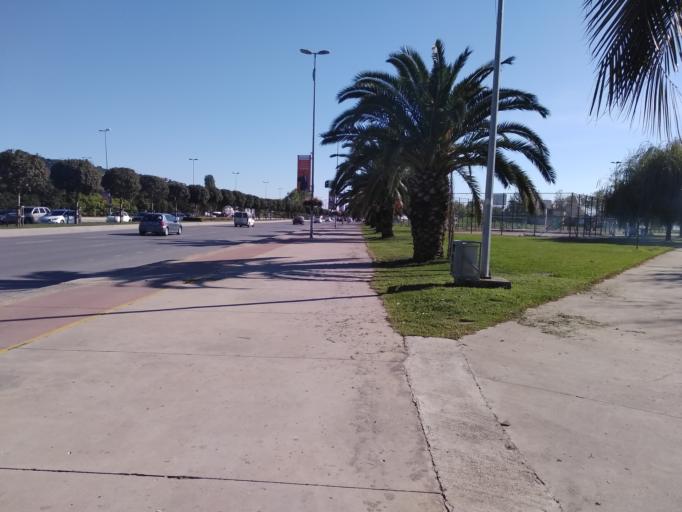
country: TR
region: Istanbul
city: Maltepe
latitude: 40.9151
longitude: 29.1323
